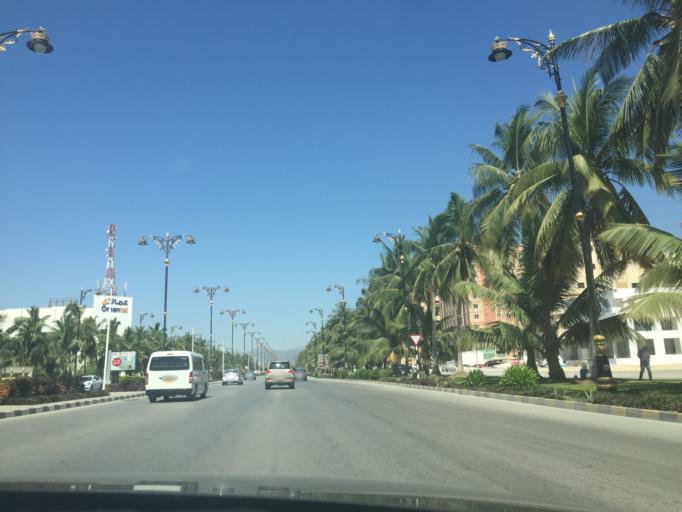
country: OM
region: Zufar
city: Salalah
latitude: 17.0183
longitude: 54.0924
